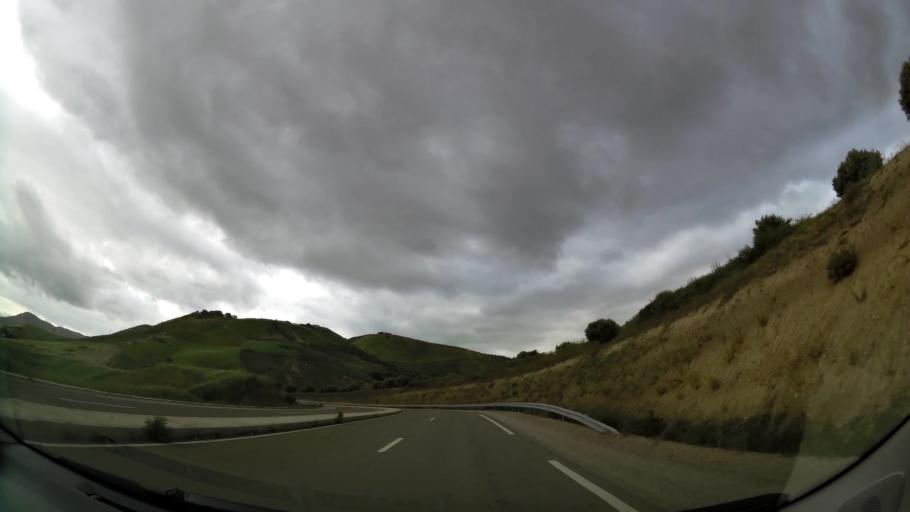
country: MA
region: Taza-Al Hoceima-Taounate
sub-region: Taza
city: Taza
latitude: 34.3211
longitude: -3.9557
